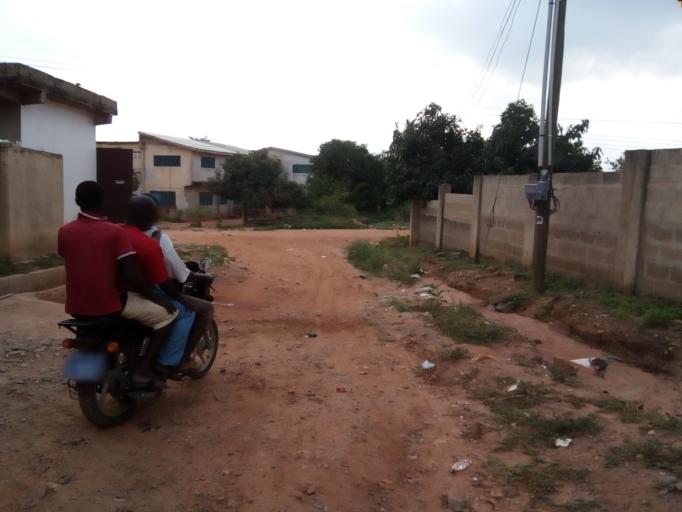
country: GH
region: Eastern
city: Nsawam
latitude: 5.7738
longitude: -0.3242
